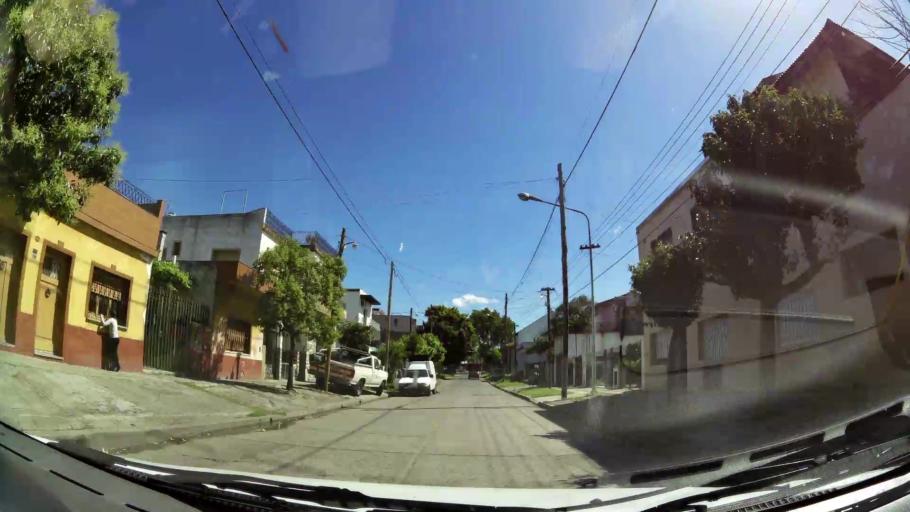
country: AR
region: Buenos Aires
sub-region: Partido de General San Martin
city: General San Martin
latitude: -34.5235
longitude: -58.5666
